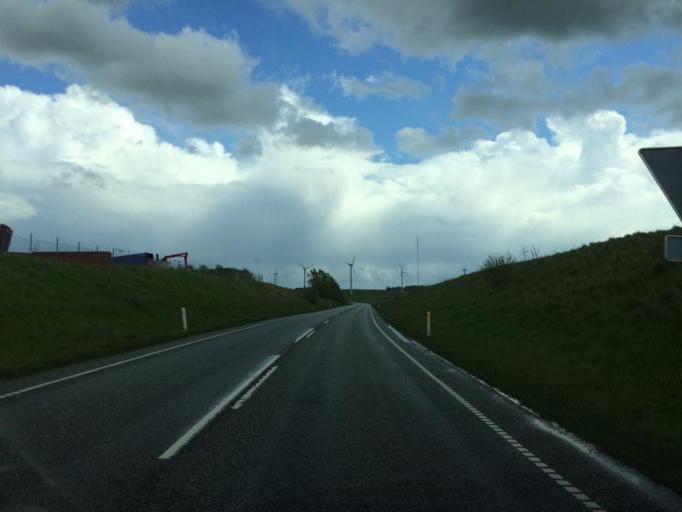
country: DK
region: Central Jutland
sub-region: Holstebro Kommune
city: Holstebro
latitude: 56.3786
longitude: 8.6376
